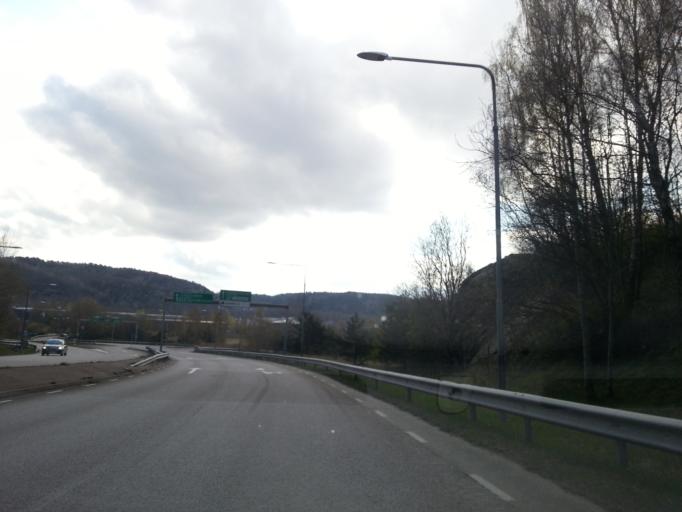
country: SE
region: Vaestra Goetaland
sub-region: Goteborg
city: Gardsten
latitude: 57.7966
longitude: 11.9998
